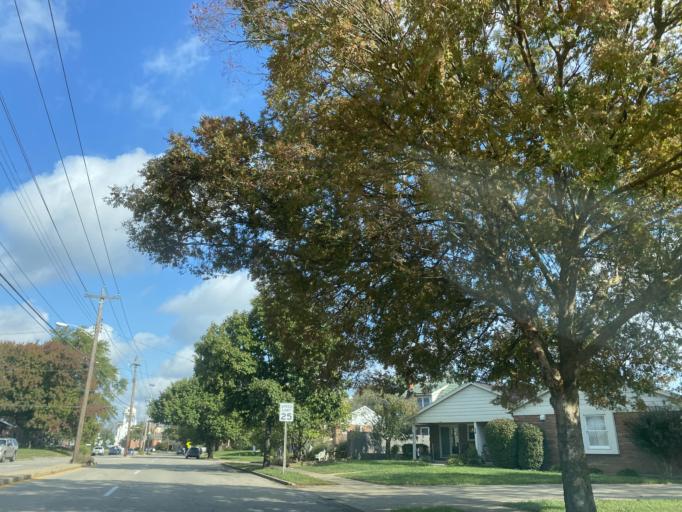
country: US
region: Kentucky
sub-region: Campbell County
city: Fort Thomas
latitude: 39.0746
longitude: -84.4471
